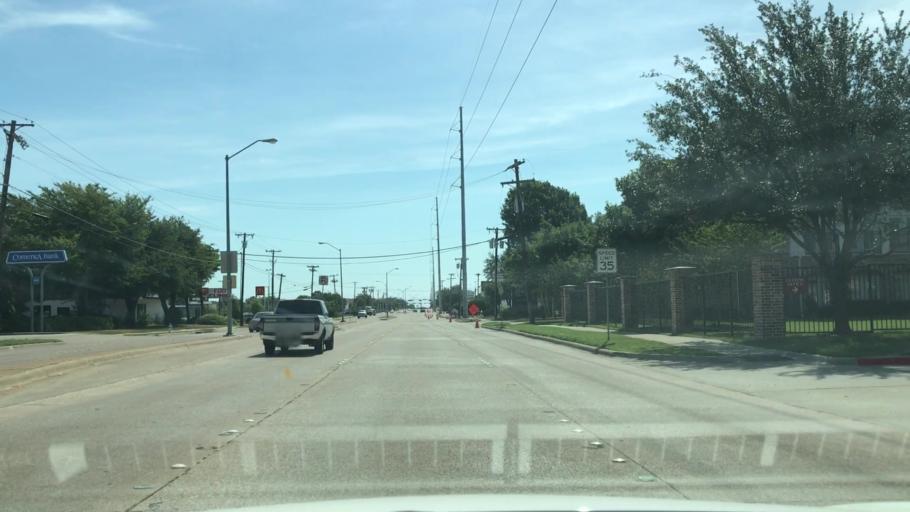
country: US
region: Texas
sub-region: Dallas County
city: Richardson
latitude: 32.9453
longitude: -96.7045
